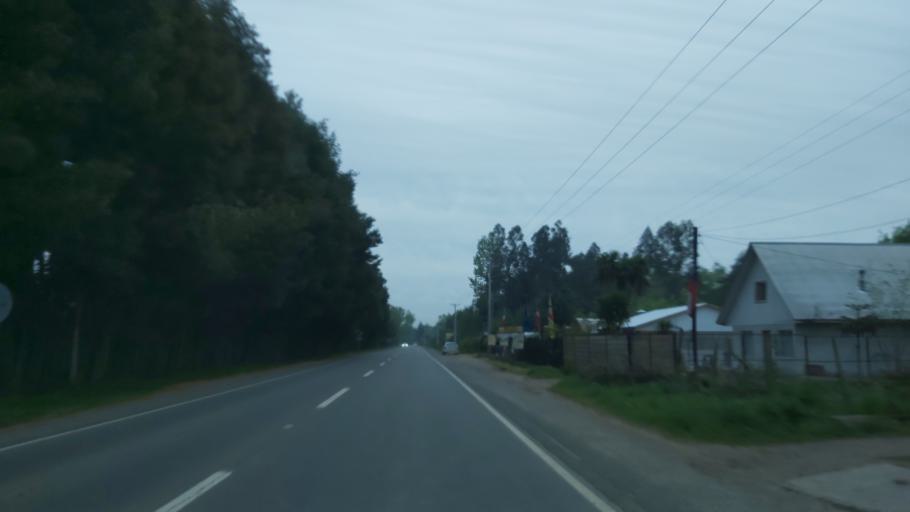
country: CL
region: Maule
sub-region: Provincia de Linares
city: Colbun
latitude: -35.7584
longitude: -71.5042
